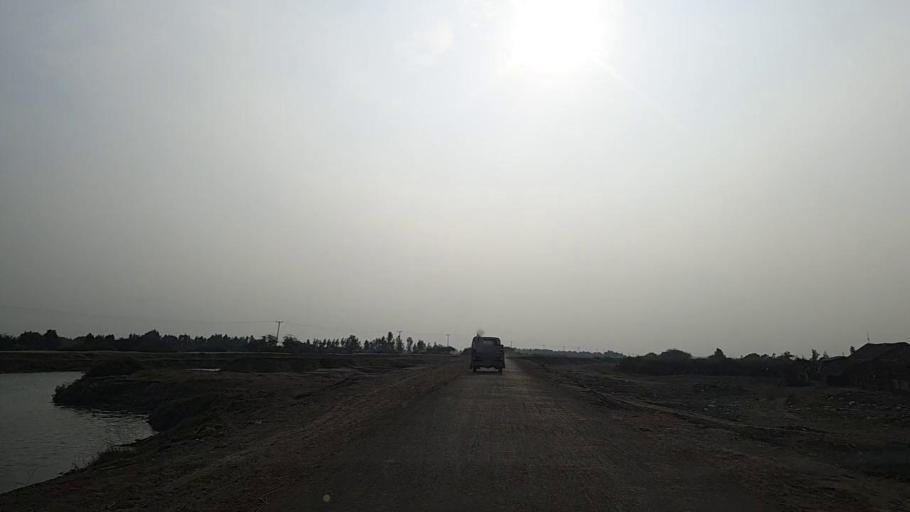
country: PK
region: Sindh
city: Mirpur Sakro
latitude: 24.6376
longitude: 67.5905
